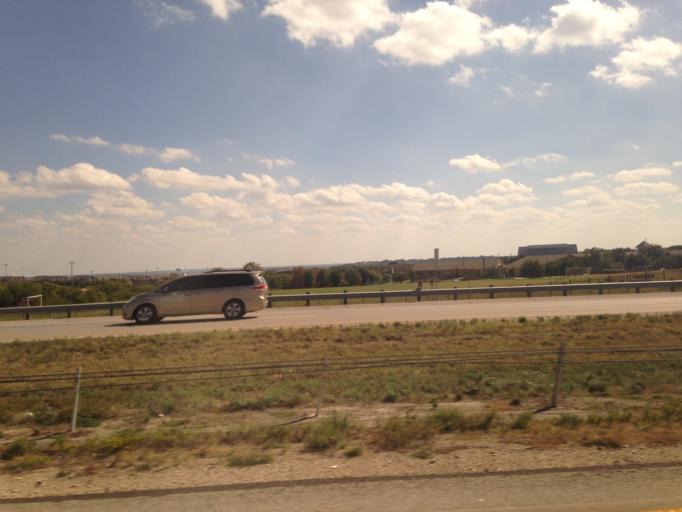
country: US
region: Texas
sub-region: Tarrant County
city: White Settlement
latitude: 32.7353
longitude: -97.4911
